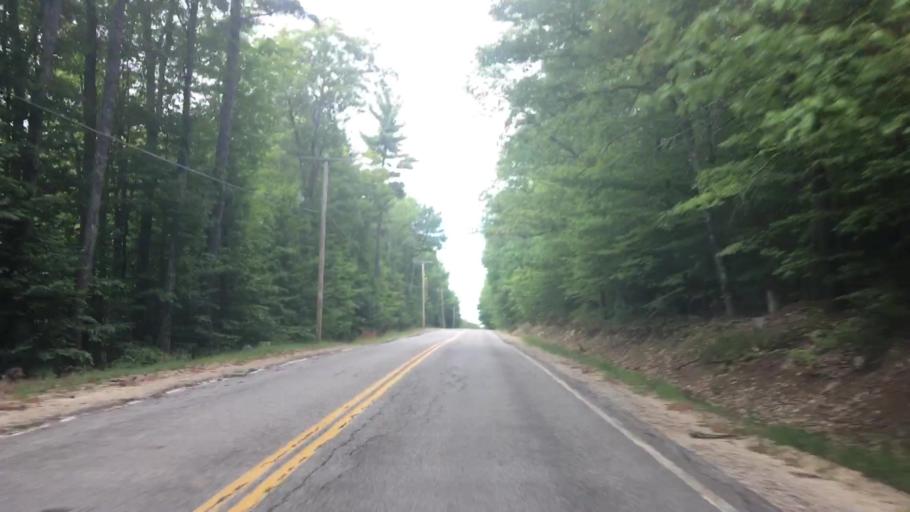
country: US
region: Maine
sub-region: Oxford County
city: Oxford
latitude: 44.0220
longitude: -70.5288
